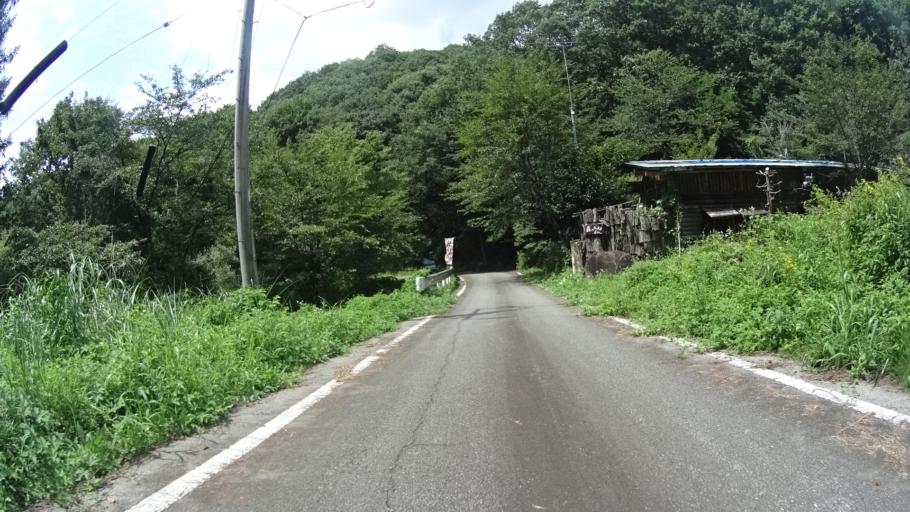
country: JP
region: Yamanashi
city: Nirasaki
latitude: 35.8802
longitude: 138.5051
